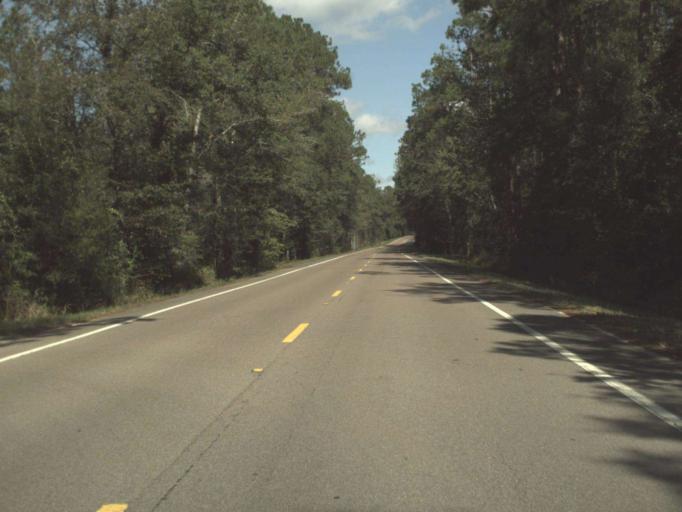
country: US
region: Florida
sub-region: Walton County
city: DeFuniak Springs
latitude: 30.9207
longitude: -86.1360
